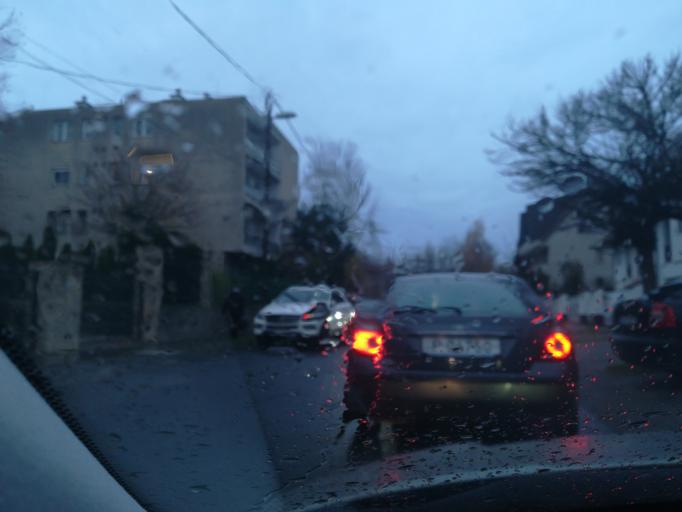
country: HU
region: Budapest
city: Budapest III. keruelet
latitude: 47.5496
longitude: 19.0342
